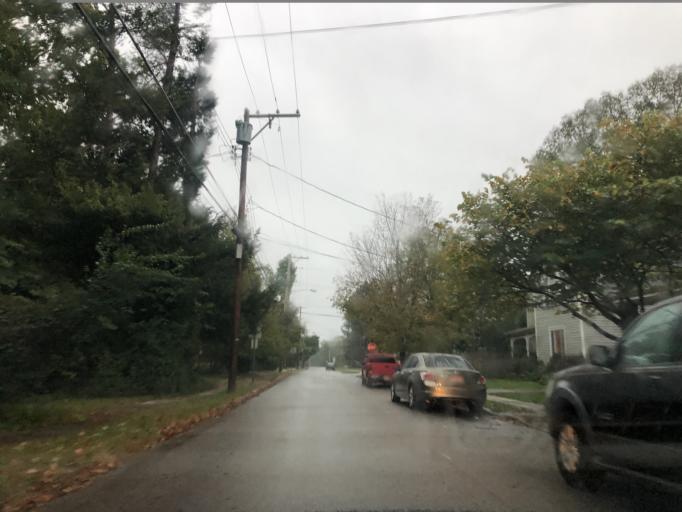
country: US
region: Ohio
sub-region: Hamilton County
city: Loveland
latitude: 39.2705
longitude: -84.2646
